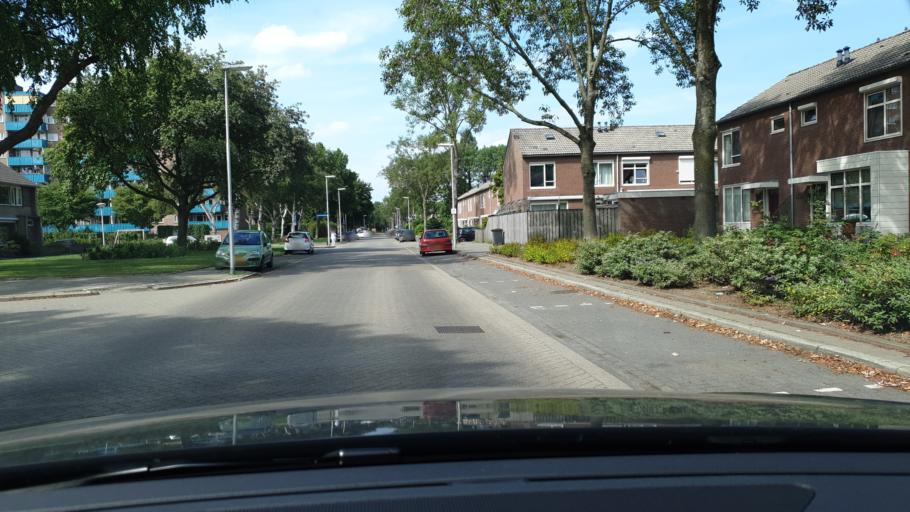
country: NL
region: North Brabant
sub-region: Gemeente Eindhoven
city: Eindhoven
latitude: 51.4777
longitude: 5.4665
